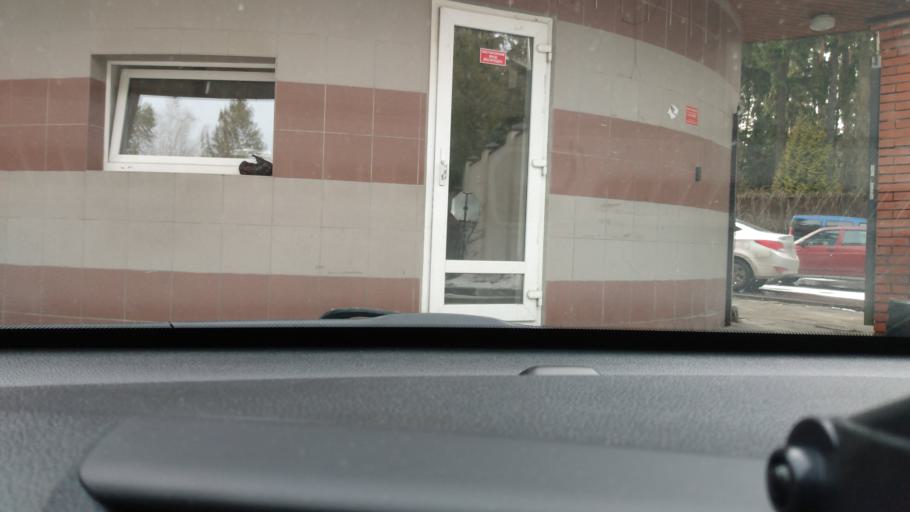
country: RU
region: Moskovskaya
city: Barvikha
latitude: 55.7292
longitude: 37.2498
